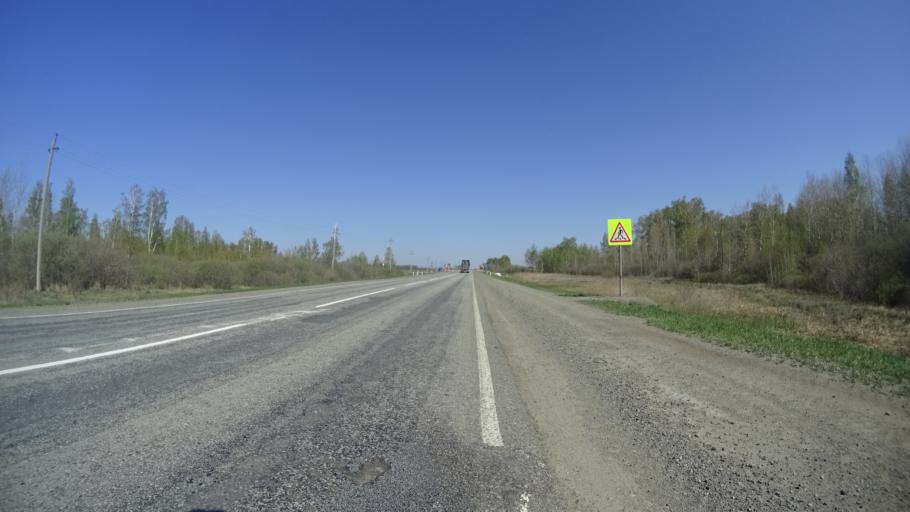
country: RU
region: Chelyabinsk
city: Troitsk
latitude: 54.1855
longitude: 61.4342
